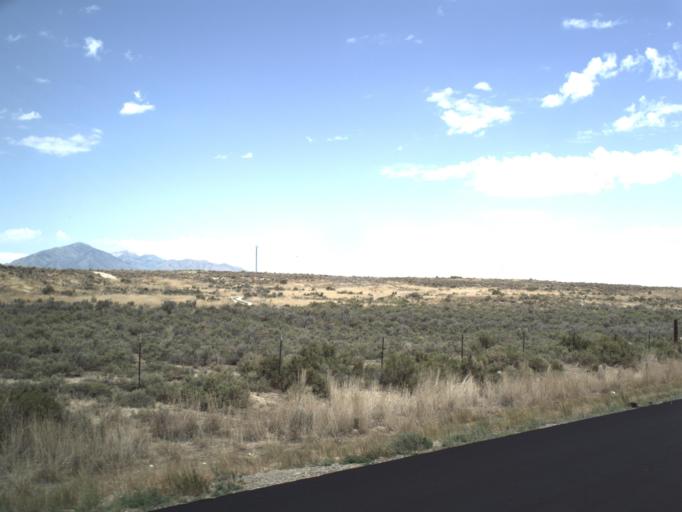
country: US
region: Utah
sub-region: Tooele County
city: Tooele
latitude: 40.1902
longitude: -112.4171
